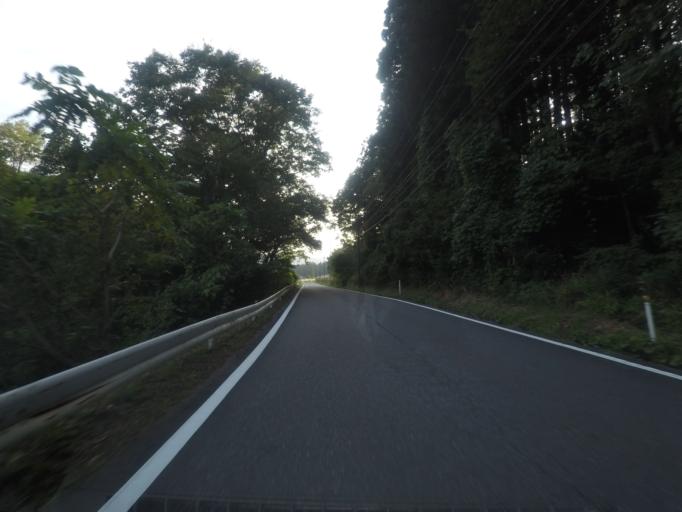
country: JP
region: Fukushima
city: Namie
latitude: 37.5651
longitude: 140.7957
